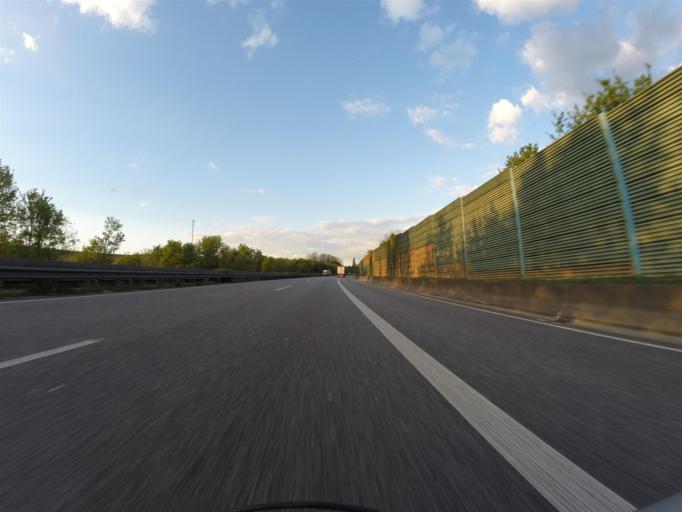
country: DE
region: Rheinland-Pfalz
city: Klein-Winternheim
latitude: 49.9418
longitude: 8.2058
